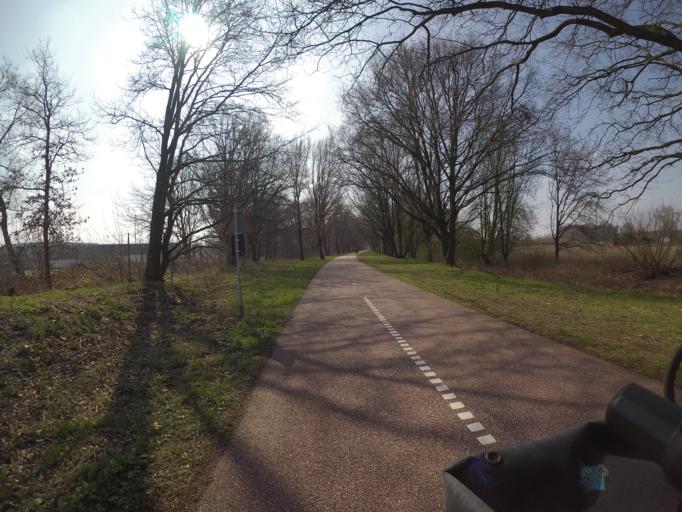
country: NL
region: North Brabant
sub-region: Gemeente Goirle
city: Goirle
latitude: 51.5375
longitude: 5.0326
